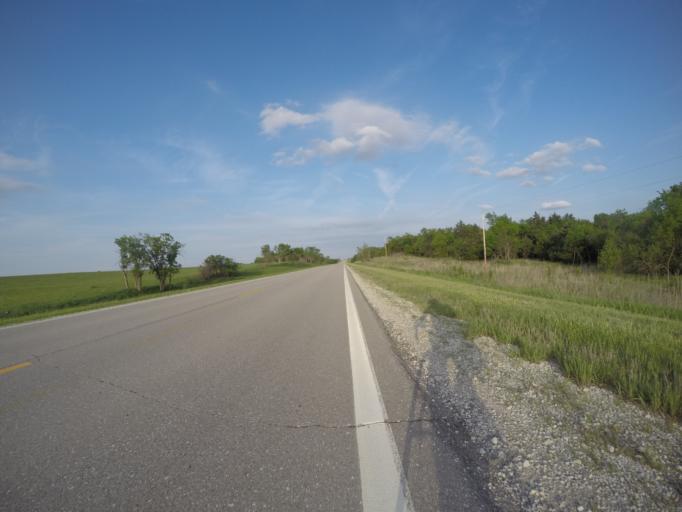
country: US
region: Kansas
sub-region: Pottawatomie County
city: Westmoreland
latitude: 39.4284
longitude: -96.5521
